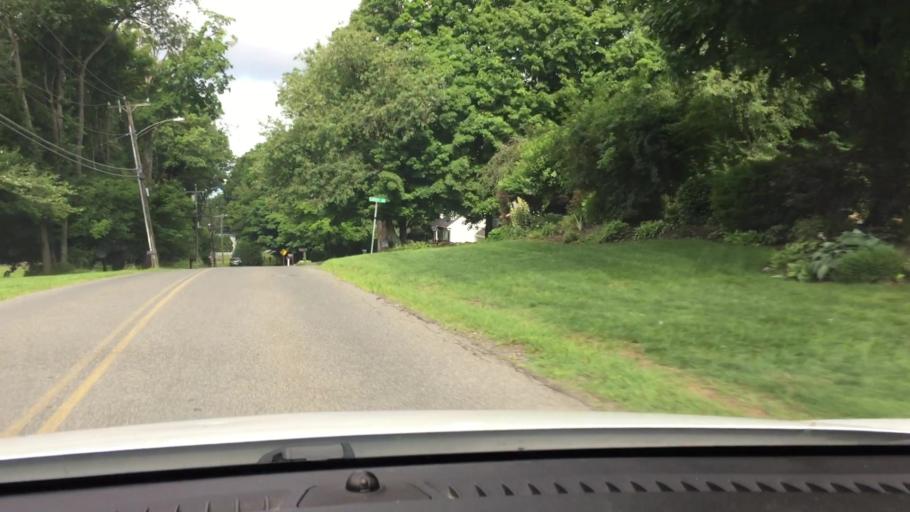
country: US
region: Massachusetts
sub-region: Berkshire County
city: Dalton
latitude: 42.4609
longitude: -73.1789
